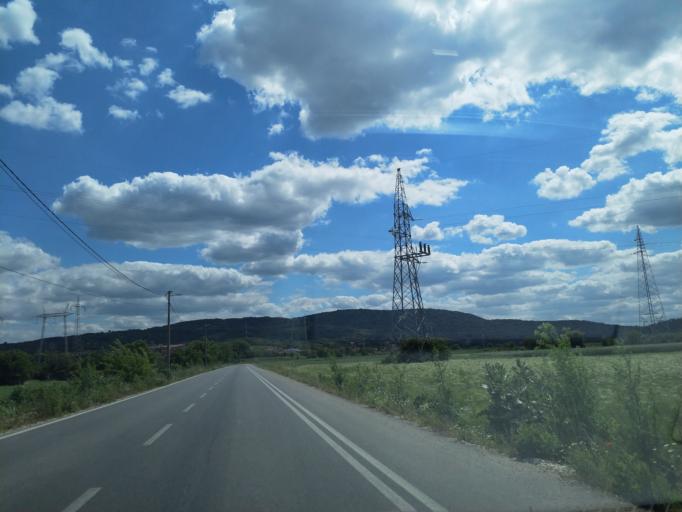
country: RS
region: Central Serbia
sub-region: Pomoravski Okrug
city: Jagodina
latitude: 43.9555
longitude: 21.2910
